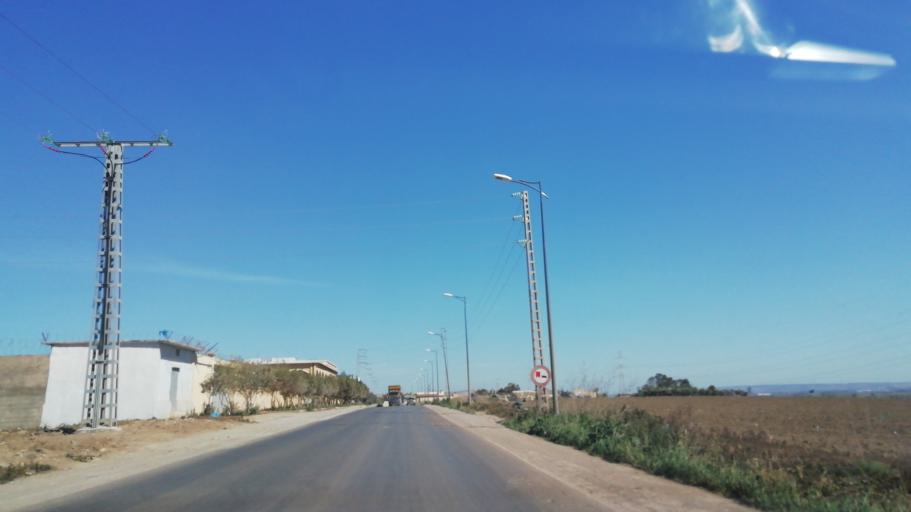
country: DZ
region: Oran
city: Es Senia
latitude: 35.5482
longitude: -0.5770
